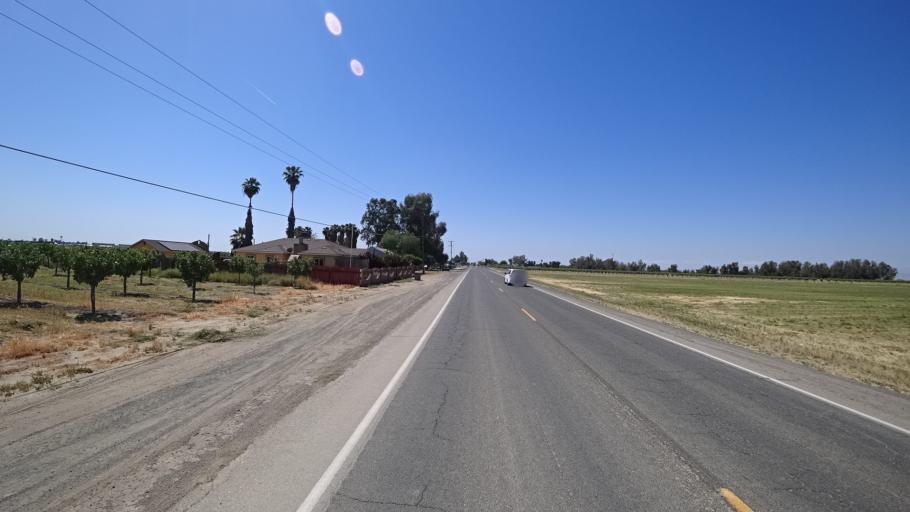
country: US
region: California
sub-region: Kings County
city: Lemoore
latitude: 36.2487
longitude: -119.7808
